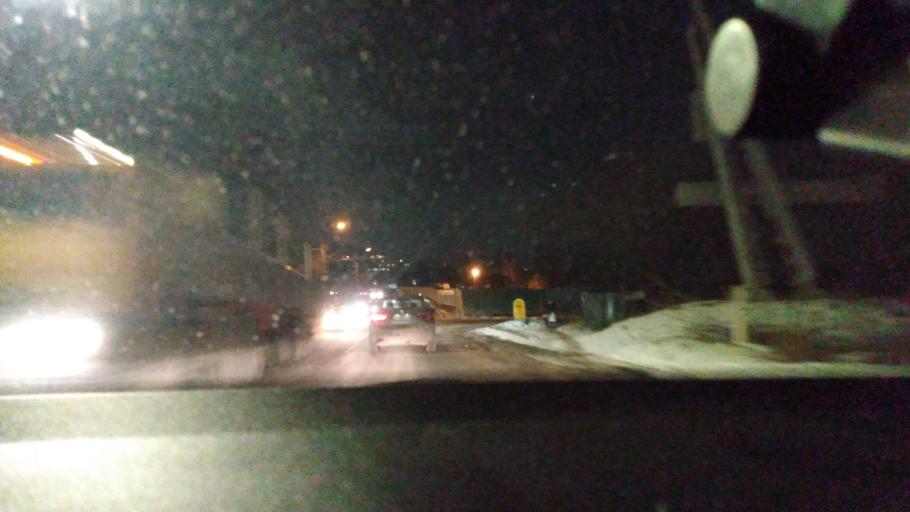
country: RU
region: Moskovskaya
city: Zheleznodorozhnyy
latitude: 55.7270
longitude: 38.0328
